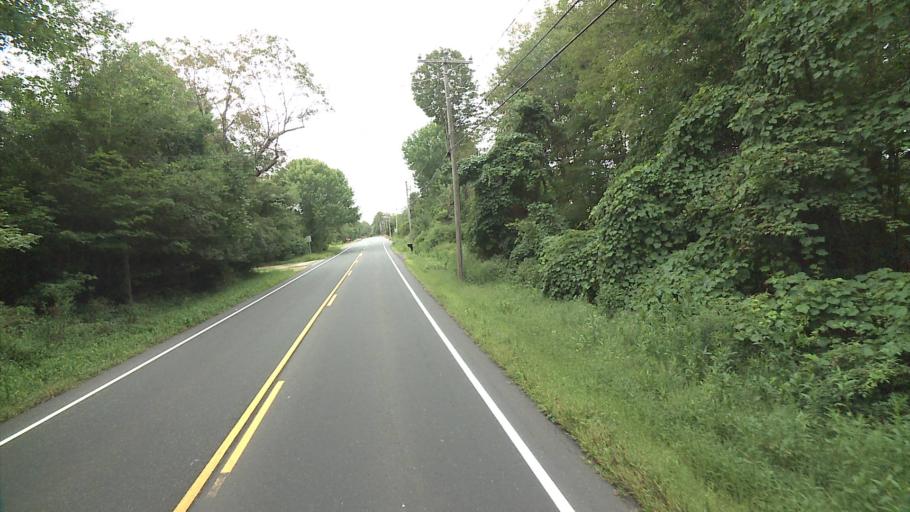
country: US
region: Connecticut
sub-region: New London County
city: Colchester
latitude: 41.5301
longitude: -72.2978
